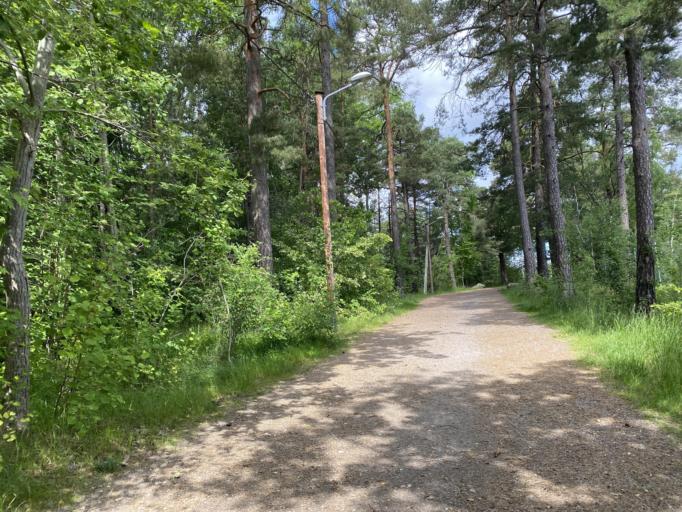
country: SE
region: Stockholm
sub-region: Jarfalla Kommun
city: Jakobsberg
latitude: 59.3752
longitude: 17.8514
